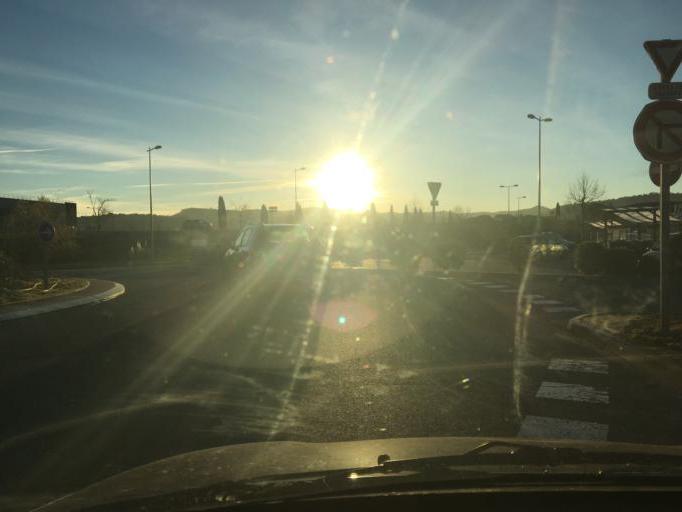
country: FR
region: Provence-Alpes-Cote d'Azur
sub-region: Departement du Var
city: Les Arcs
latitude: 43.4520
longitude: 6.4907
